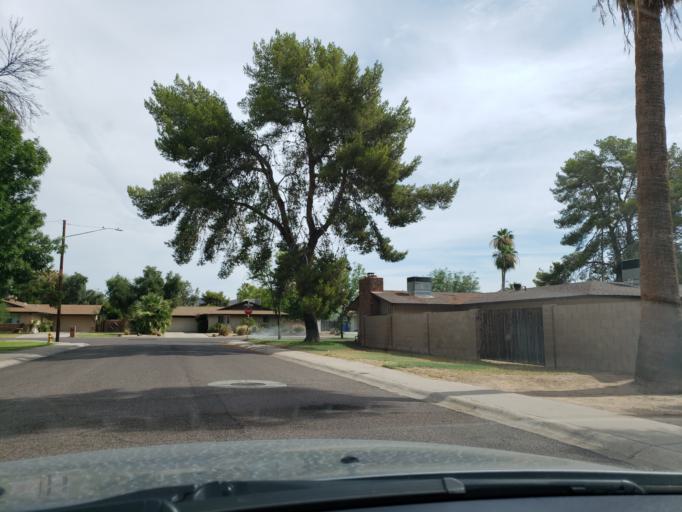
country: US
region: Arizona
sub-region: Maricopa County
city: Glendale
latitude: 33.5598
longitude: -112.0945
